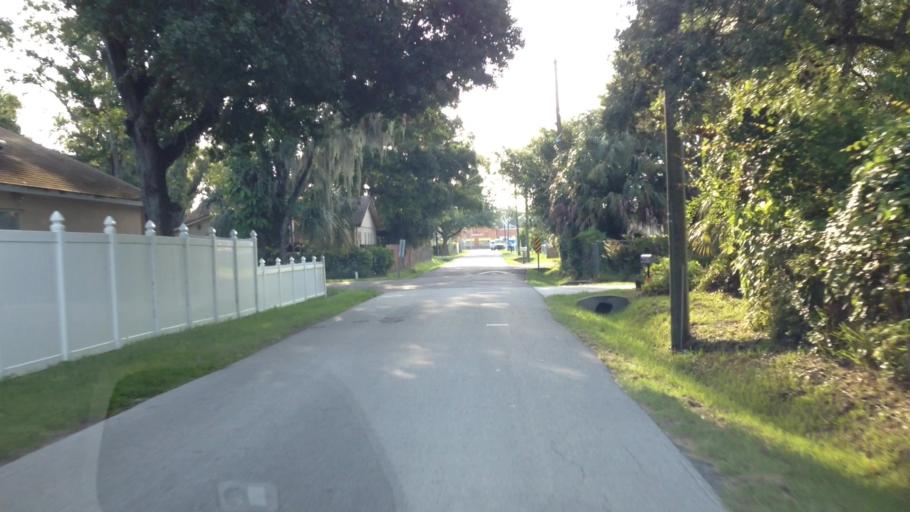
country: US
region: Florida
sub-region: Hillsborough County
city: Tampa
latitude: 27.8737
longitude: -82.5088
